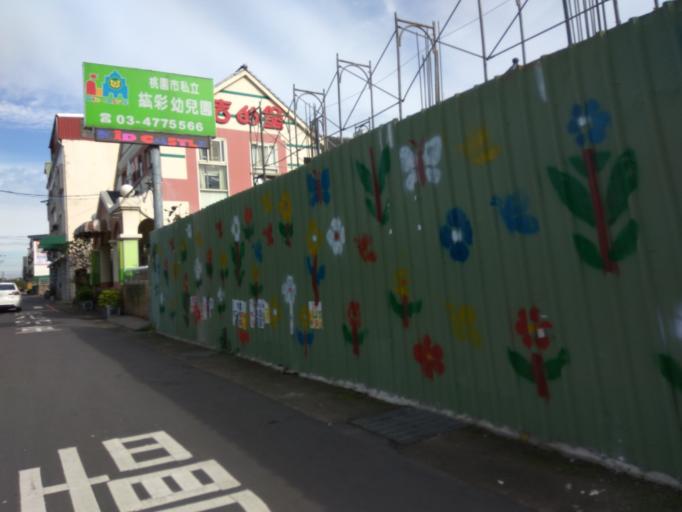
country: TW
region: Taiwan
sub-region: Hsinchu
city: Zhubei
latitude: 24.9743
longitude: 121.1034
